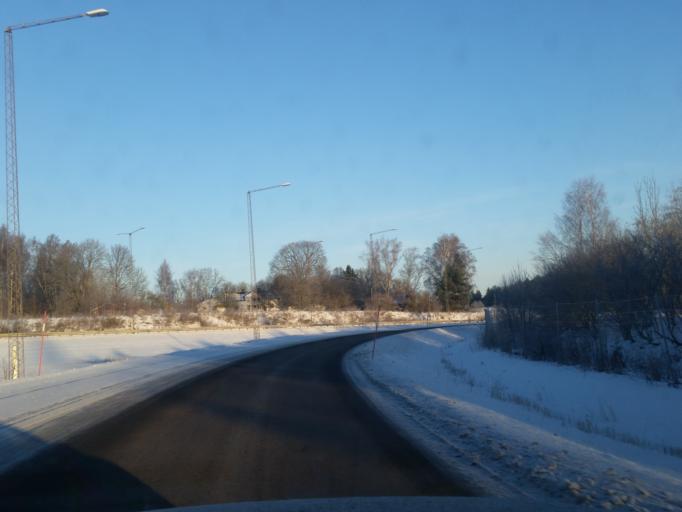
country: SE
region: Stockholm
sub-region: Sodertalje Kommun
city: Soedertaelje
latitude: 59.1880
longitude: 17.5658
